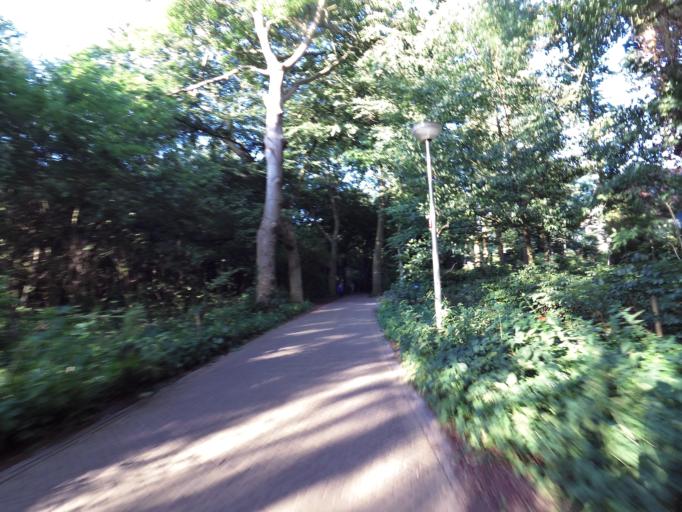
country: NL
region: Gelderland
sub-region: Gemeente Doetinchem
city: Doetinchem
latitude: 51.9738
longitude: 6.2791
